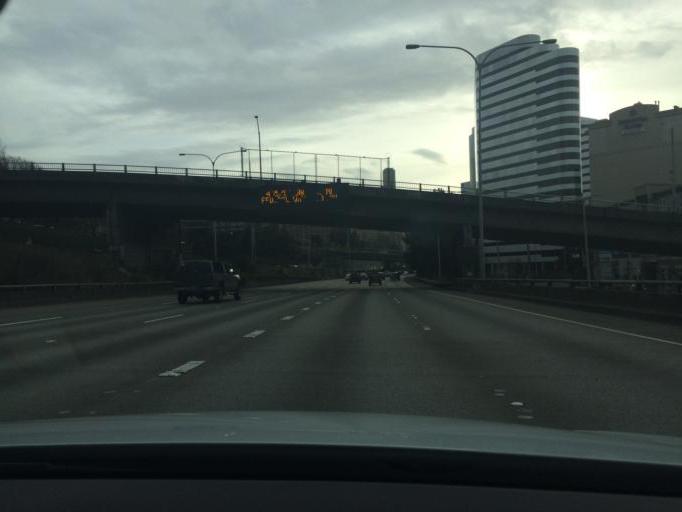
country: US
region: Washington
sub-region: King County
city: Seattle
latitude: 47.6191
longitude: -122.3287
